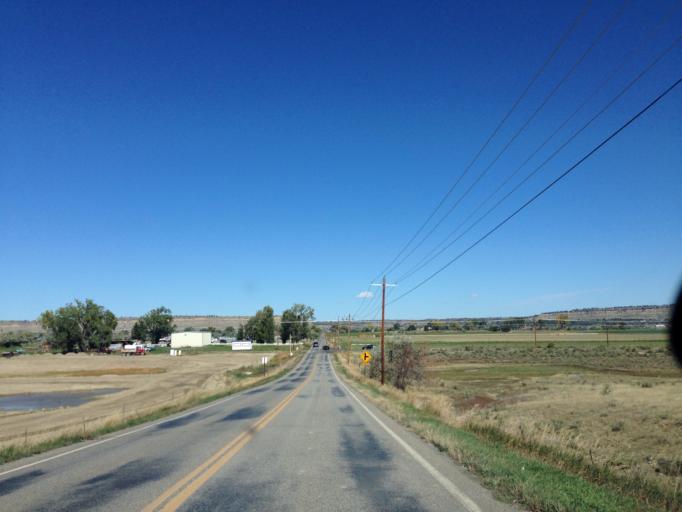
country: US
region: Montana
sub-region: Yellowstone County
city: Laurel
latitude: 45.7674
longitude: -108.6795
